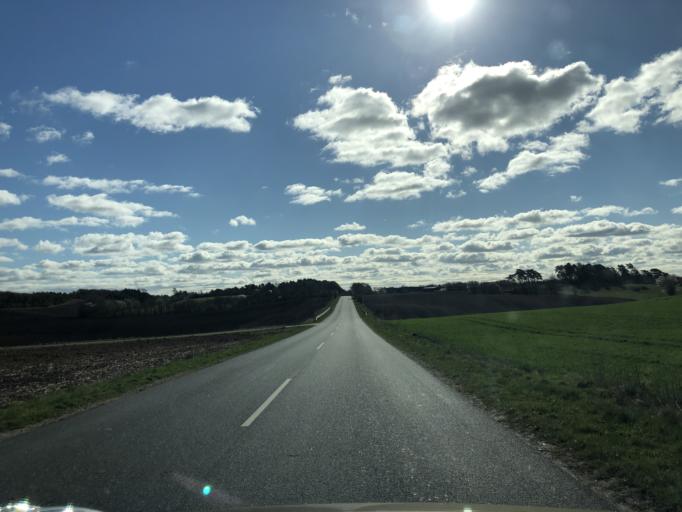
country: DK
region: North Denmark
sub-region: Vesthimmerland Kommune
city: Alestrup
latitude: 56.6144
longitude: 9.5215
